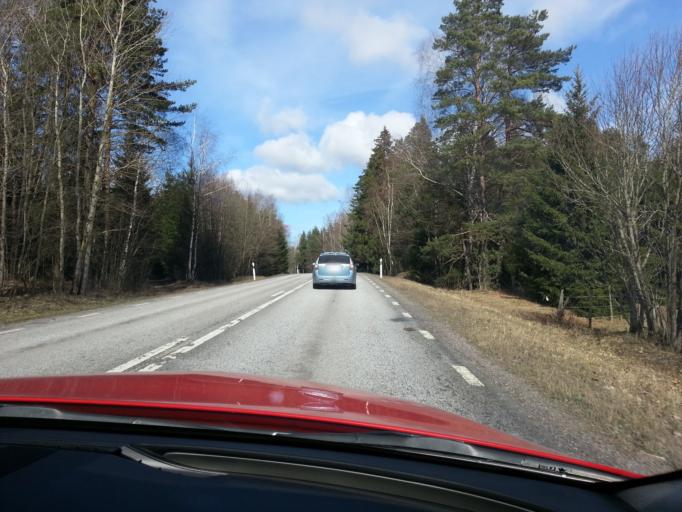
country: SE
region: Uppsala
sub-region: Osthammars Kommun
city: Gimo
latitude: 60.0964
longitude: 18.1246
